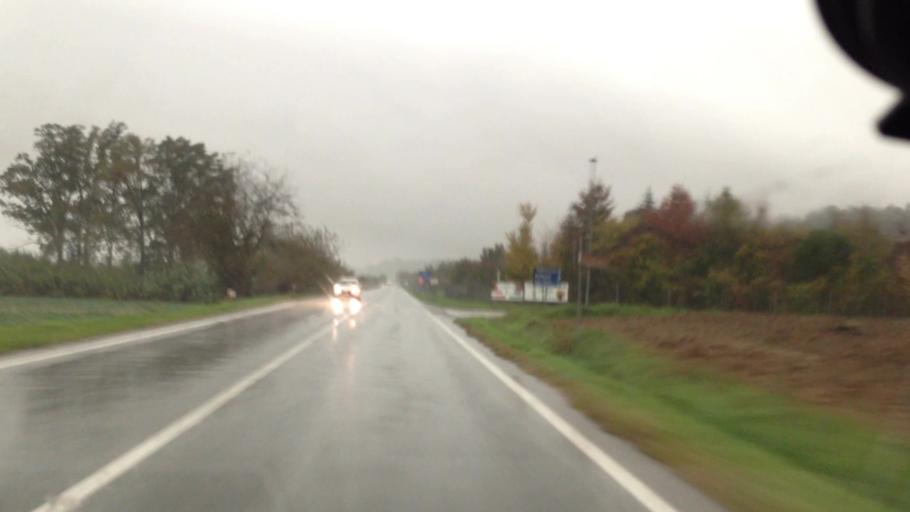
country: IT
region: Piedmont
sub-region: Provincia di Asti
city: Castello di Annone
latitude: 44.8969
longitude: 8.2961
